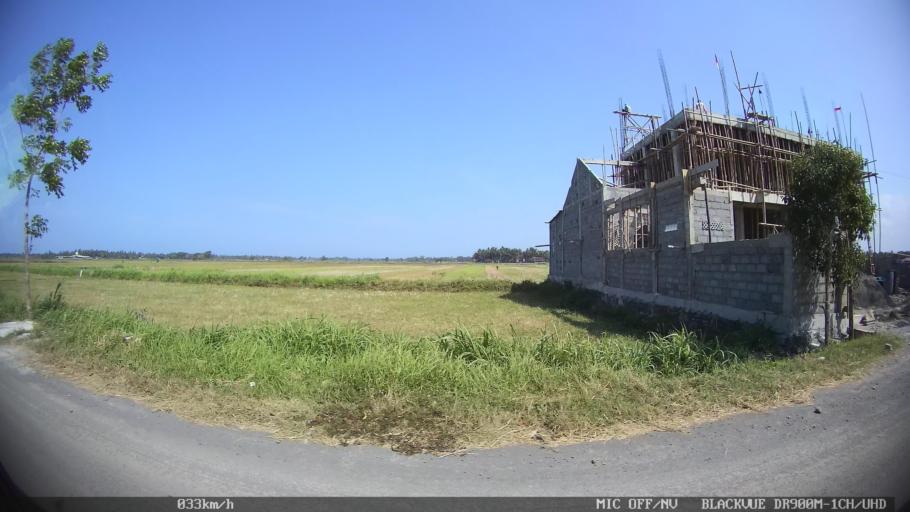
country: ID
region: Daerah Istimewa Yogyakarta
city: Srandakan
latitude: -7.9656
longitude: 110.2130
